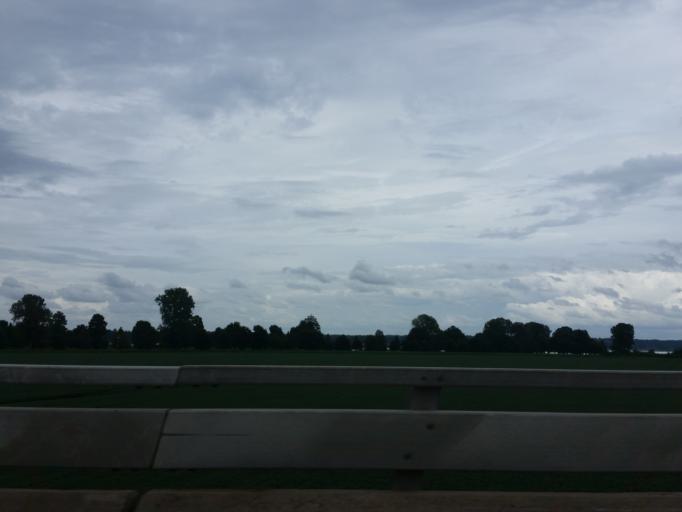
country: US
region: Illinois
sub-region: Alexander County
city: Cairo
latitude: 36.9838
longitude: -89.1494
